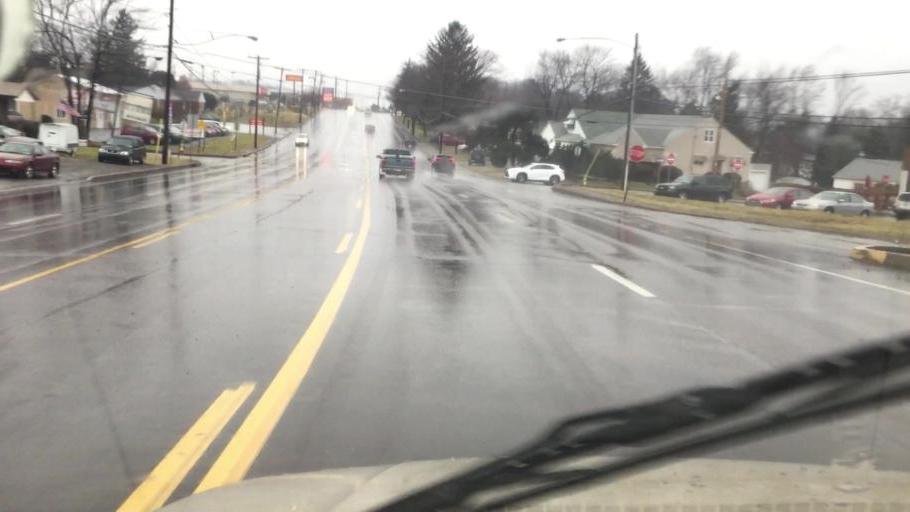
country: US
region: Pennsylvania
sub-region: Luzerne County
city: West Hazleton
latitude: 40.9666
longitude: -75.9991
